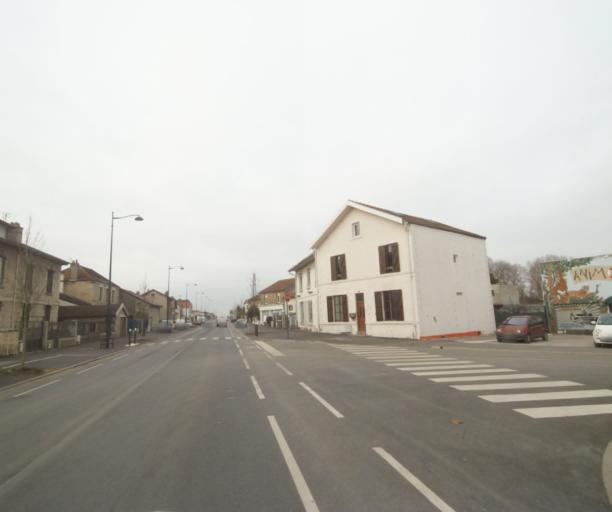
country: FR
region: Champagne-Ardenne
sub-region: Departement de la Haute-Marne
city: Saint-Dizier
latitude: 48.6383
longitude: 4.9294
